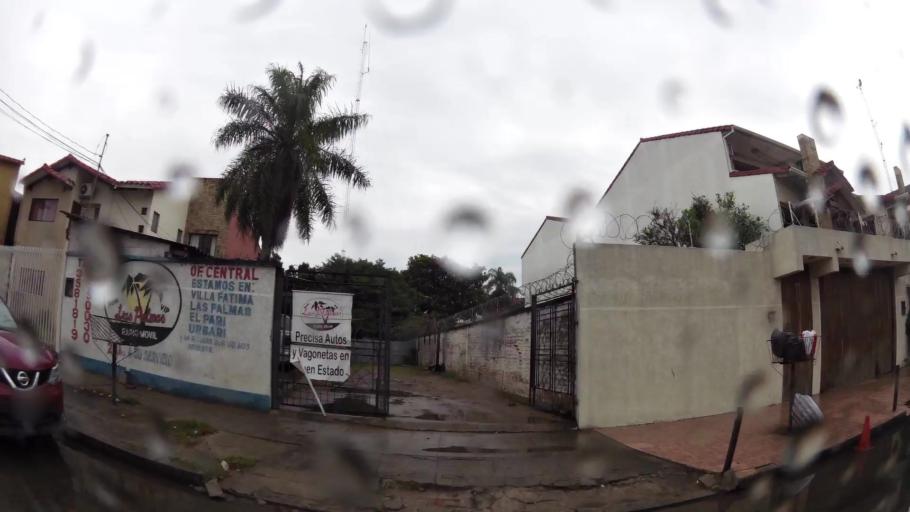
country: BO
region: Santa Cruz
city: Santa Cruz de la Sierra
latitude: -17.8072
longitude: -63.2010
